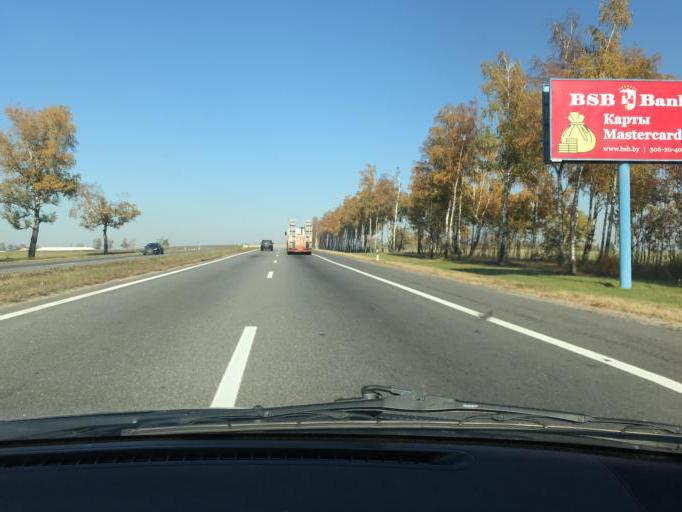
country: BY
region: Minsk
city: Yubilyeyny
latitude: 53.7823
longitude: 27.5258
